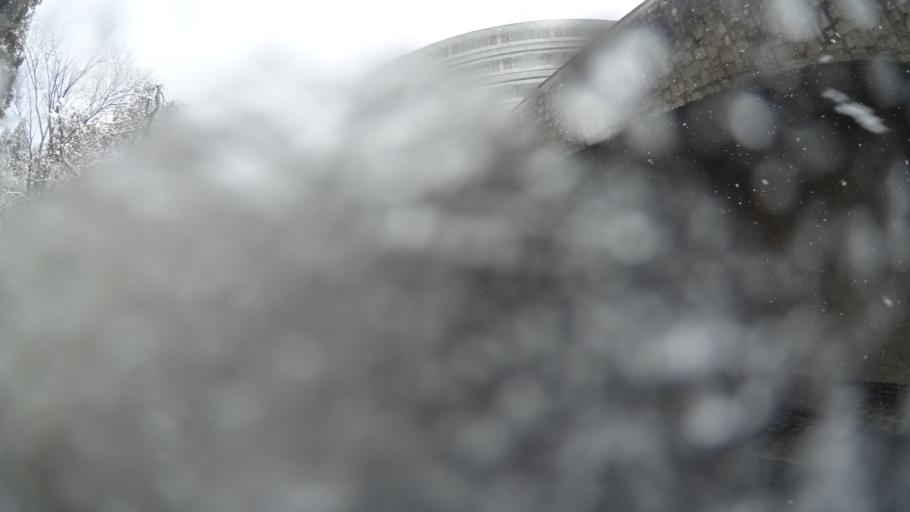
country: JP
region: Kyoto
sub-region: Kyoto-shi
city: Kamigyo-ku
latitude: 35.0628
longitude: 135.7802
